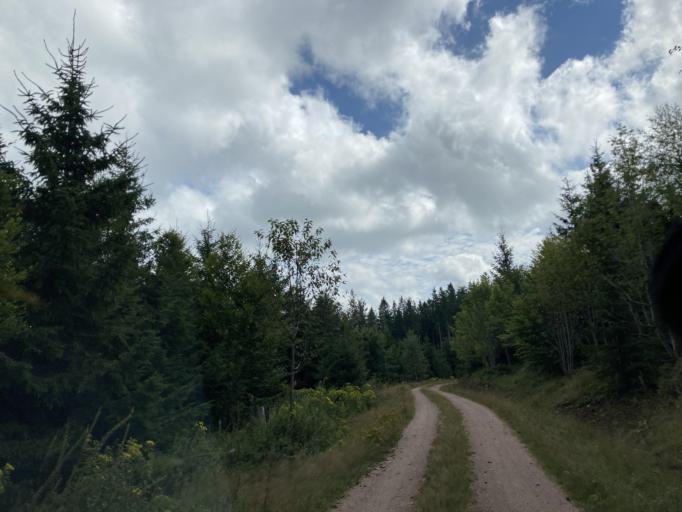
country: DE
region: Baden-Wuerttemberg
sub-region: Freiburg Region
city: Schonach im Schwarzwald
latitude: 48.1531
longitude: 8.1407
